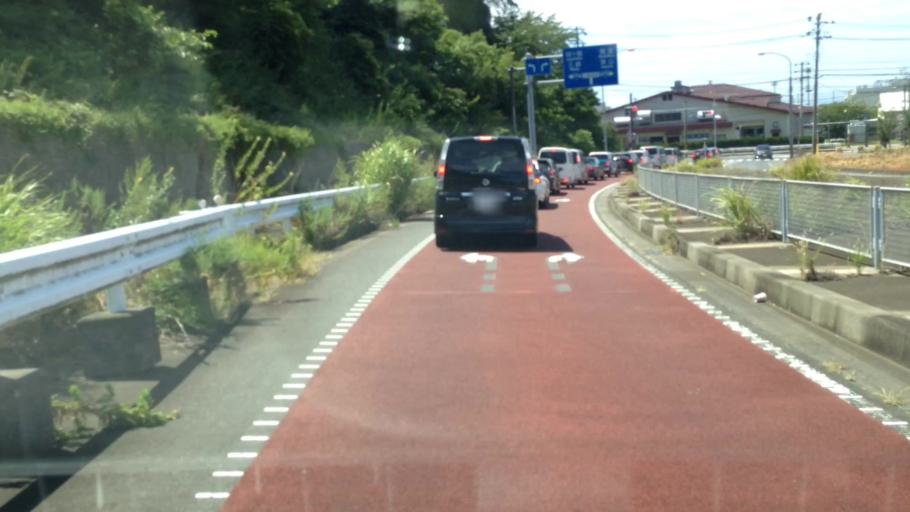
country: JP
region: Kanagawa
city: Miura
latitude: 35.2107
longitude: 139.6340
